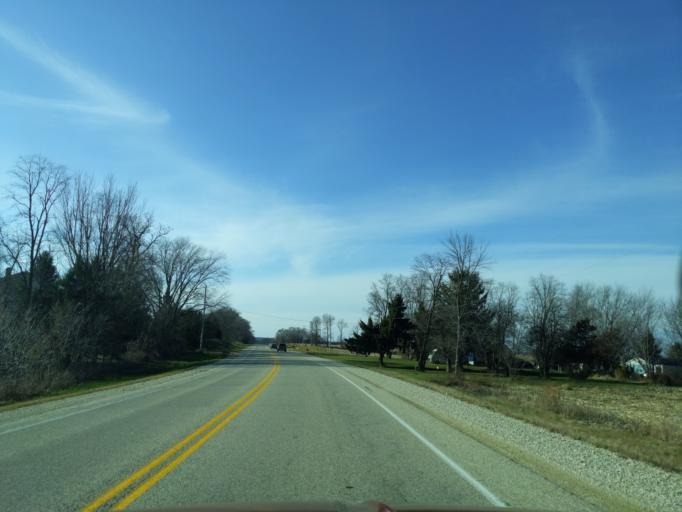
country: US
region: Wisconsin
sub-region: Rock County
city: Milton
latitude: 42.8243
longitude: -88.9615
